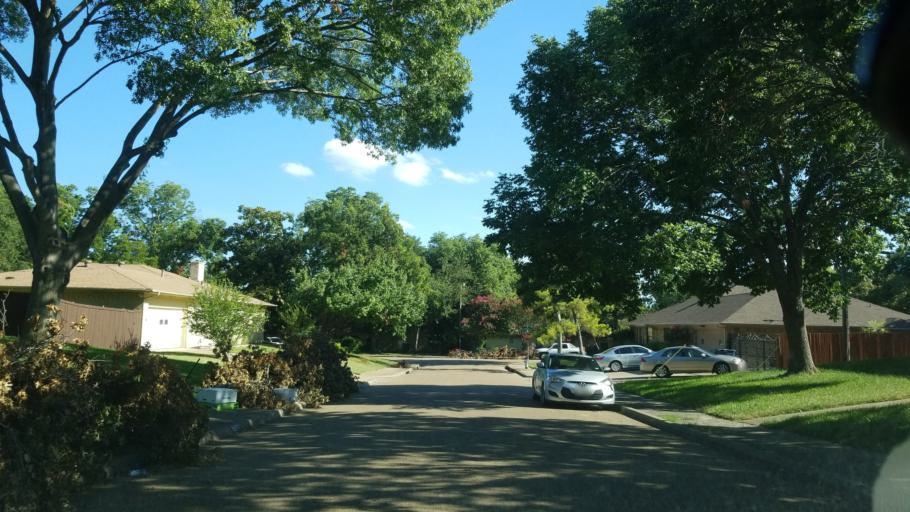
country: US
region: Texas
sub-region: Dallas County
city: Highland Park
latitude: 32.7870
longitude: -96.7113
